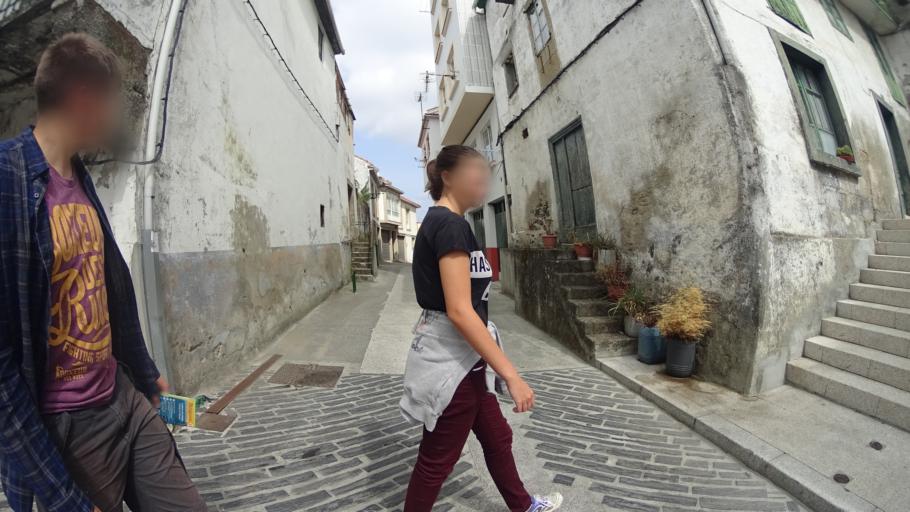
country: ES
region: Galicia
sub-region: Provincia da Coruna
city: Betanzos
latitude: 43.2810
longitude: -8.2129
